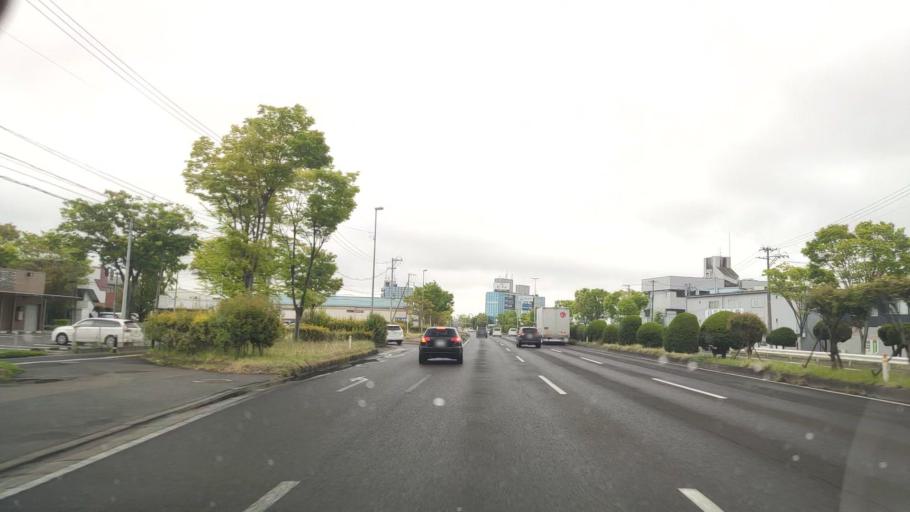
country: JP
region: Miyagi
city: Sendai-shi
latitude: 38.2534
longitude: 140.9314
